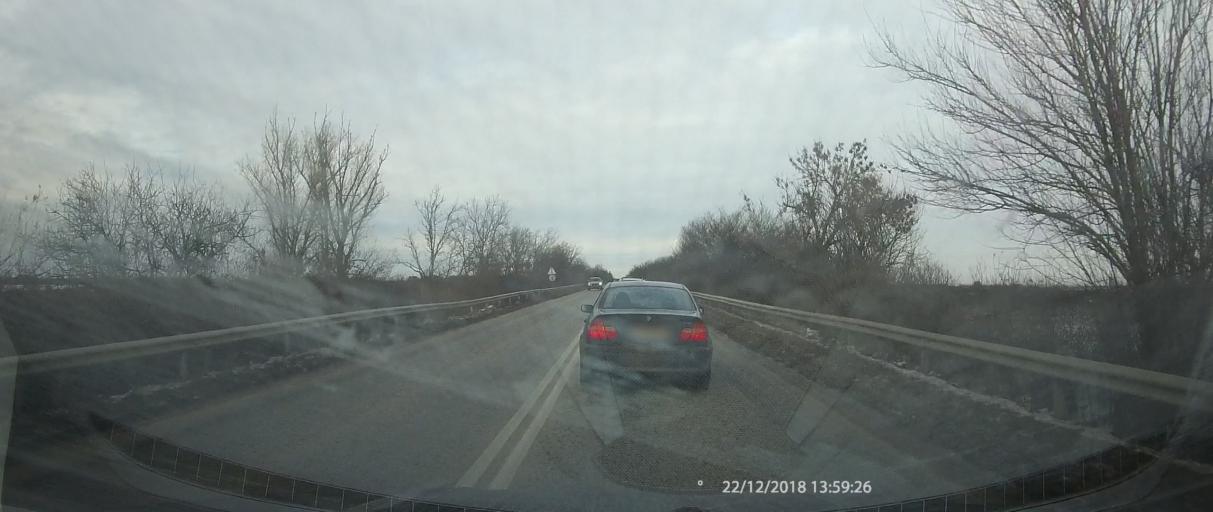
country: BG
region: Pleven
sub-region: Obshtina Dolni Dubnik
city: Dolni Dubnik
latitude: 43.3475
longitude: 24.3439
